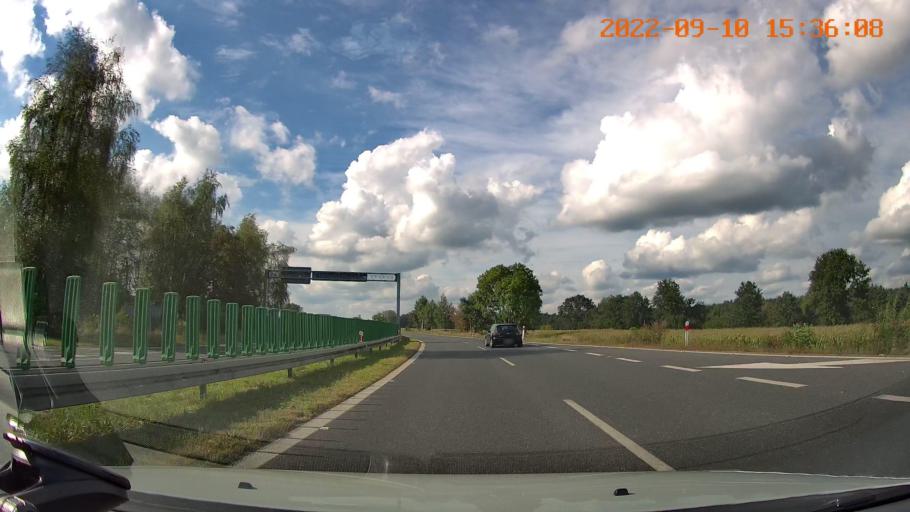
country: PL
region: Silesian Voivodeship
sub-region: Powiat bierunsko-ledzinski
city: Bierun
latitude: 50.1048
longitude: 19.0936
